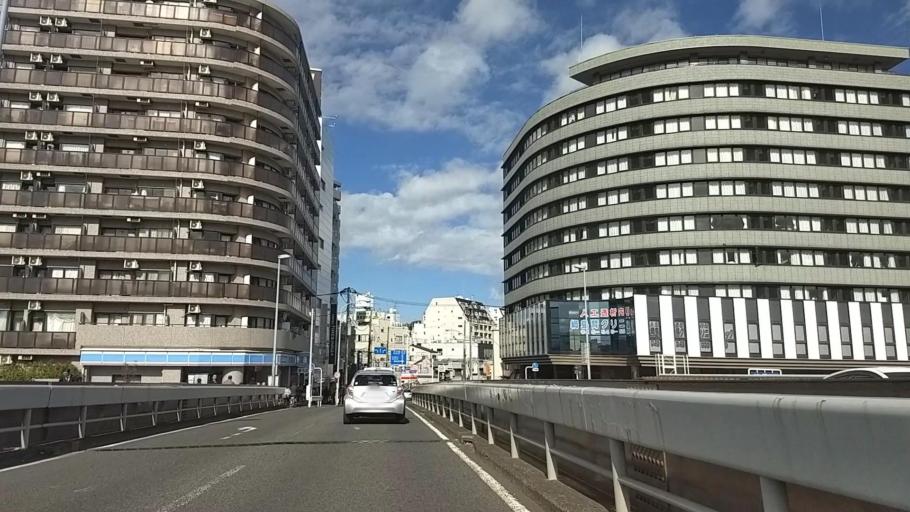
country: JP
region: Kanagawa
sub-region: Kawasaki-shi
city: Kawasaki
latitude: 35.5343
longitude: 139.6347
